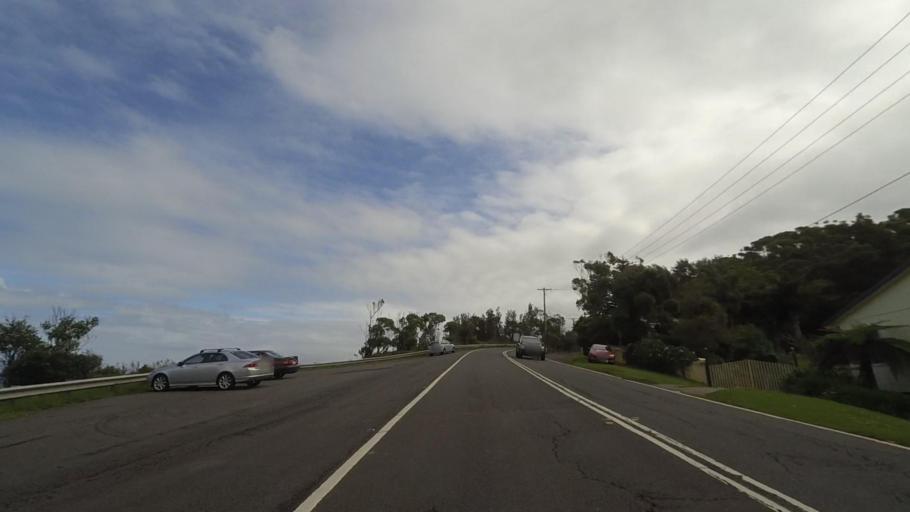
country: AU
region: New South Wales
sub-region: Wollongong
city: Helensburgh
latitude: -34.2145
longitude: 151.0064
